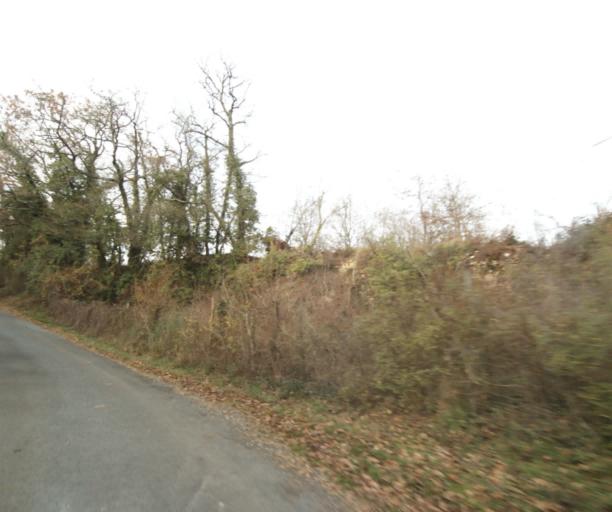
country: FR
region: Poitou-Charentes
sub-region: Departement de la Charente-Maritime
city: Fontcouverte
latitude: 45.7762
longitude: -0.5861
